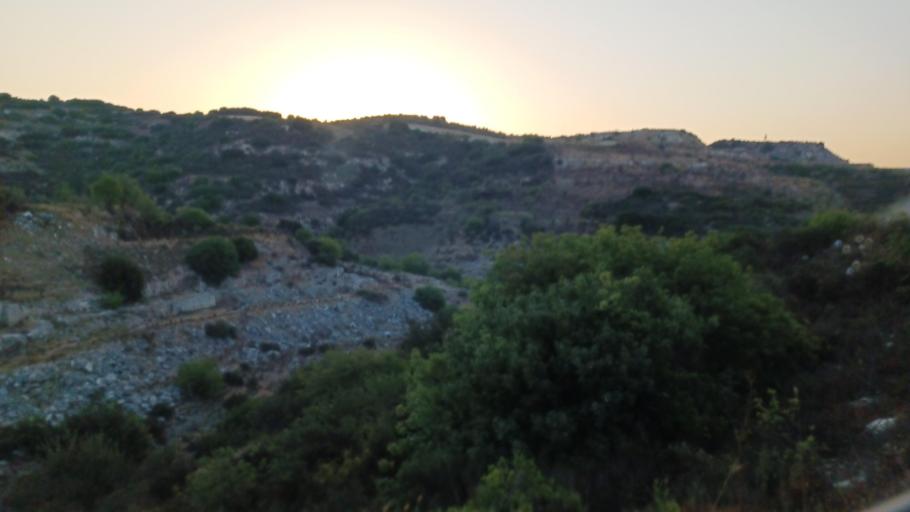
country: CY
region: Pafos
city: Mesogi
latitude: 34.8724
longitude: 32.5307
